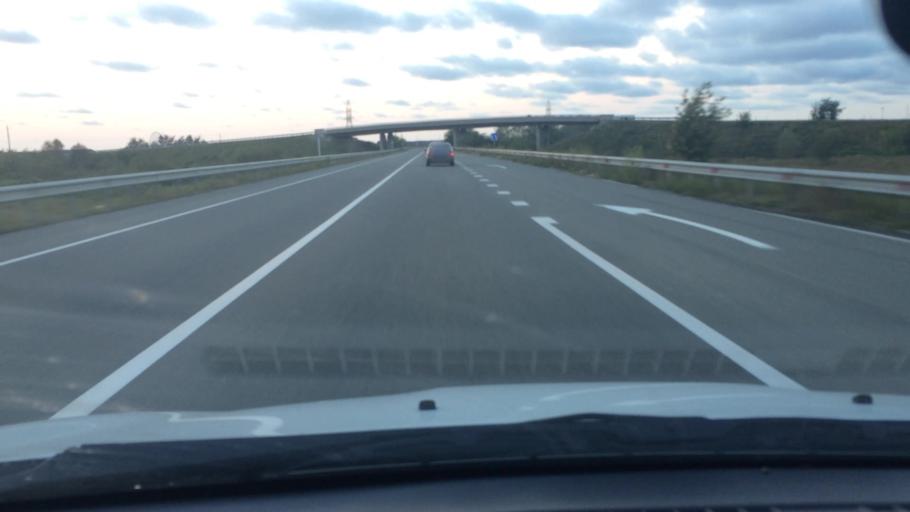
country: GE
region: Ajaria
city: Ochkhamuri
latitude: 41.8972
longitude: 41.7990
